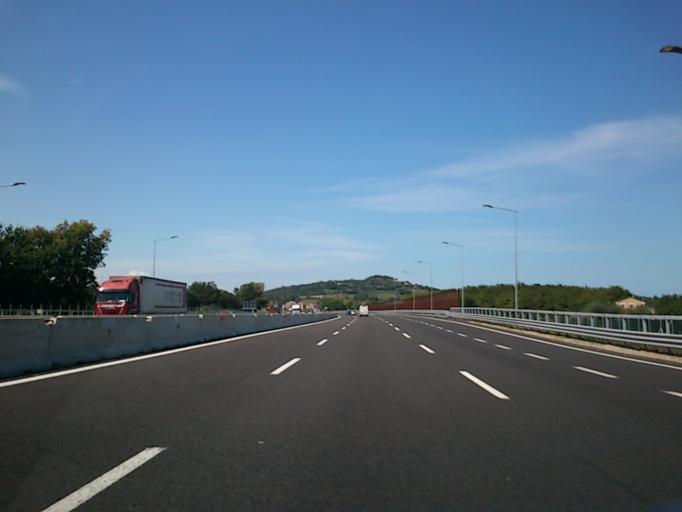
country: IT
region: The Marches
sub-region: Provincia di Pesaro e Urbino
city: Pesaro
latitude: 43.8954
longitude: 12.8777
